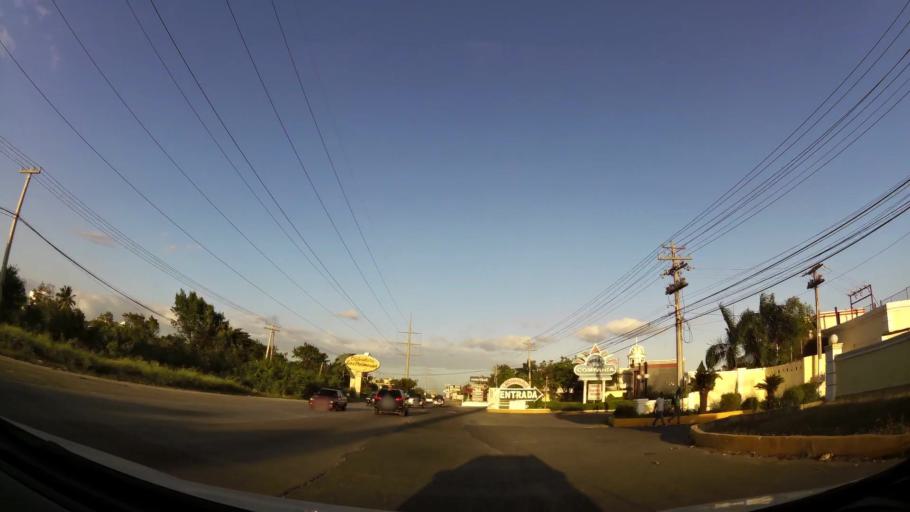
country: DO
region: Santo Domingo
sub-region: Santo Domingo
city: Santo Domingo Este
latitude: 18.4904
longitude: -69.8212
